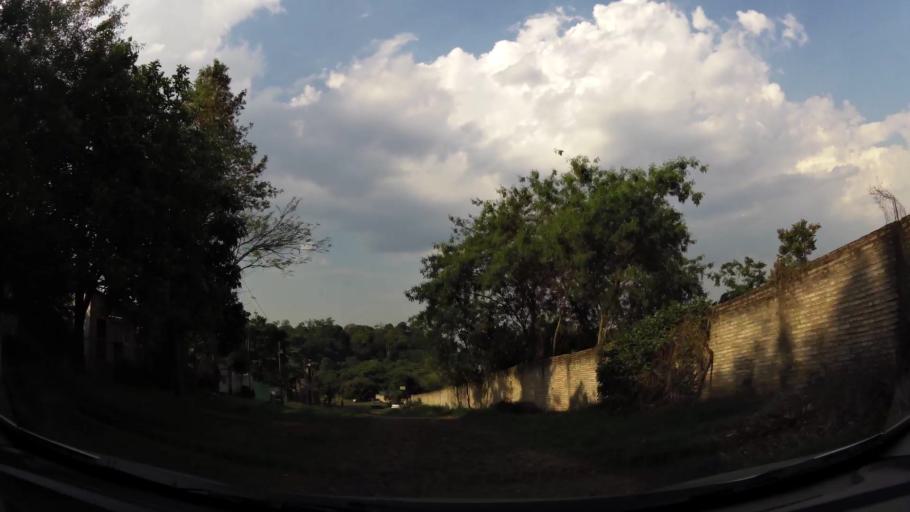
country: PY
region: Alto Parana
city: Presidente Franco
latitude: -25.5267
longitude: -54.6287
